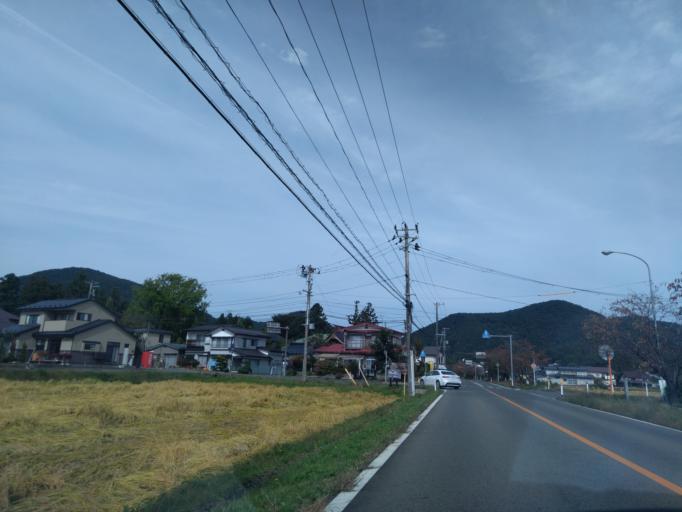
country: JP
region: Iwate
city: Hanamaki
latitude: 39.4431
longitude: 141.0764
